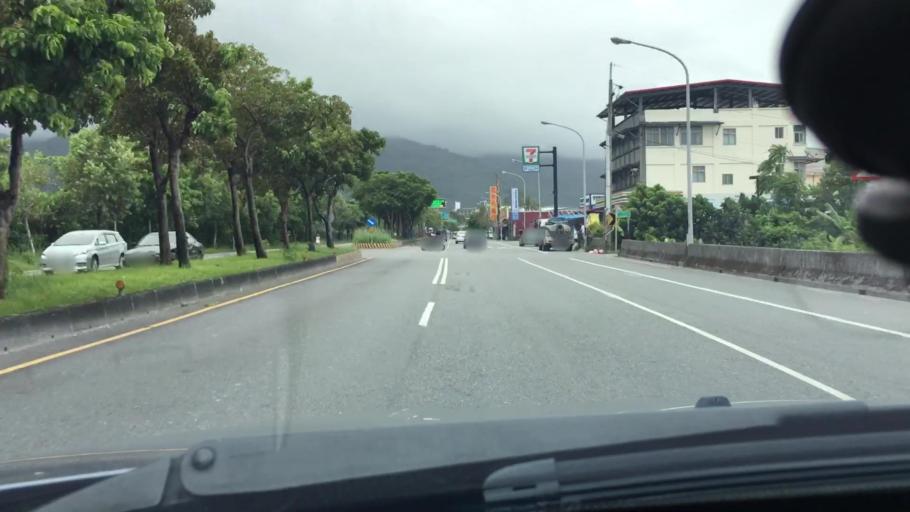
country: TW
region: Taiwan
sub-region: Yilan
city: Yilan
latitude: 24.8120
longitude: 121.7674
